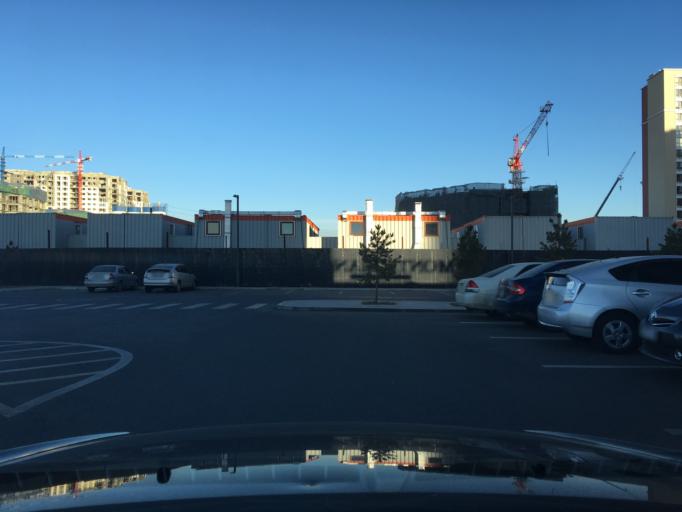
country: MN
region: Ulaanbaatar
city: Ulaanbaatar
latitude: 47.8922
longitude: 106.9233
